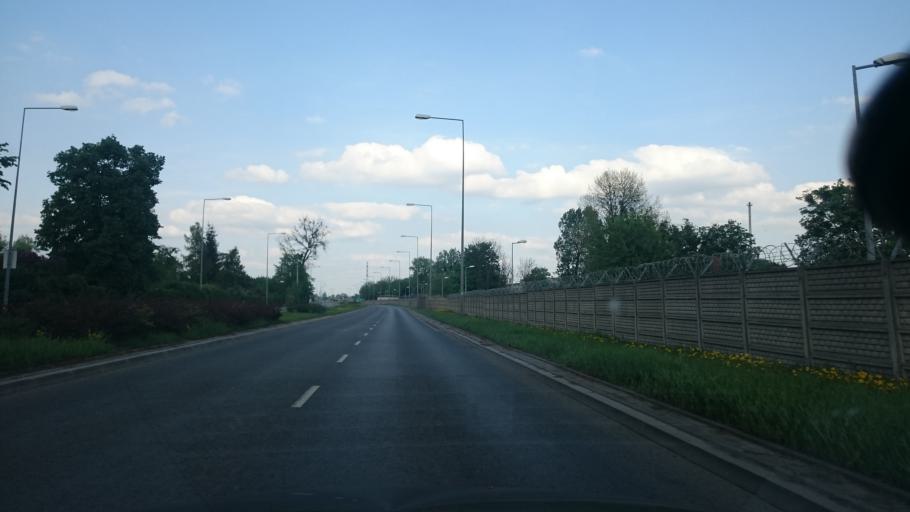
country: PL
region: Kujawsko-Pomorskie
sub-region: Grudziadz
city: Grudziadz
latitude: 53.4734
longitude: 18.7726
